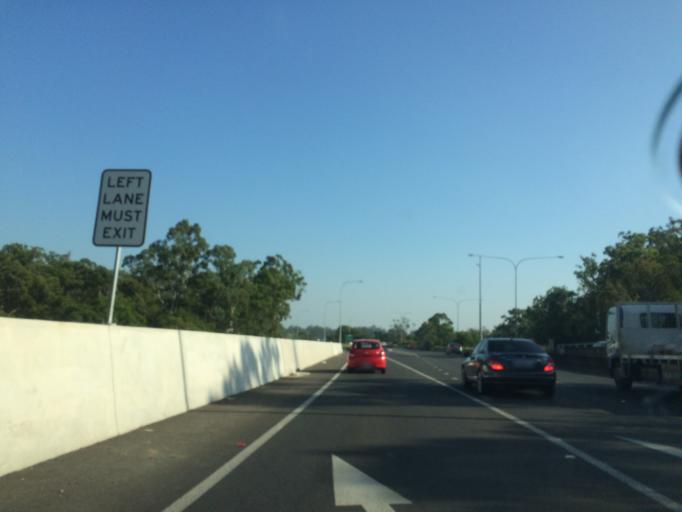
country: AU
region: Queensland
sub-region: Brisbane
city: Taringa
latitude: -27.4996
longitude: 152.9632
